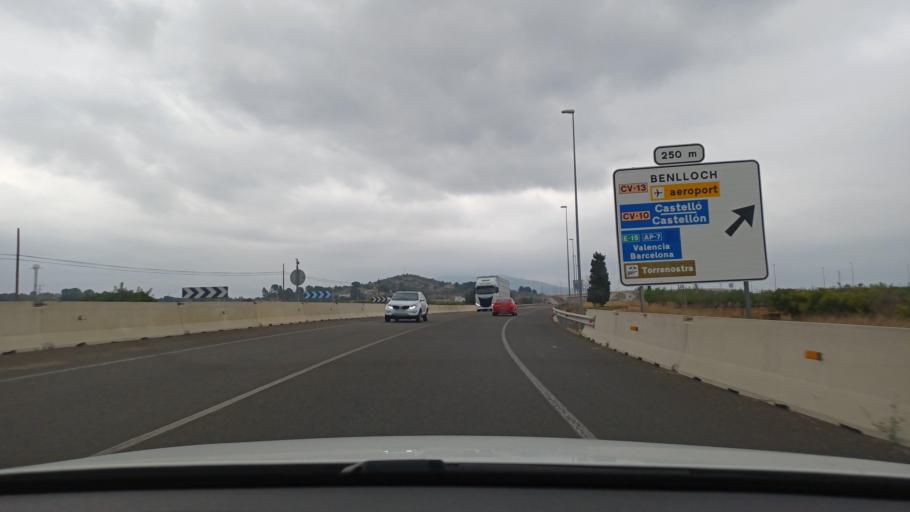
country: ES
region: Valencia
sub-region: Provincia de Castello
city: Torreblanca
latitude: 40.2240
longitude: 0.2063
